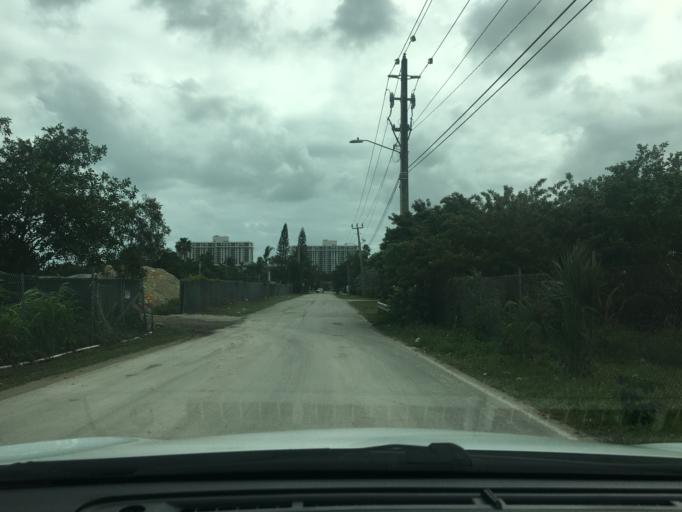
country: US
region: Florida
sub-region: Miami-Dade County
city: Biscayne Park
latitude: 25.8801
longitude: -80.1699
